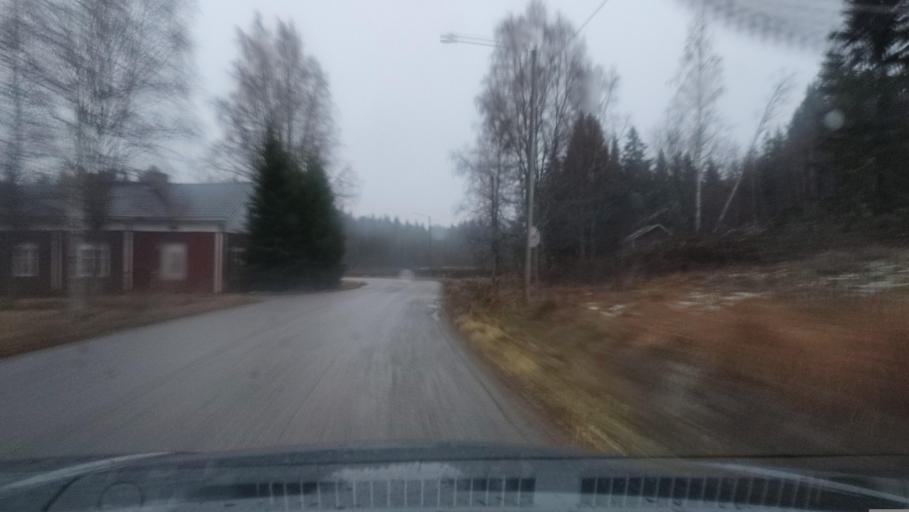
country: FI
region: Southern Ostrobothnia
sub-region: Suupohja
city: Karijoki
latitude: 62.1361
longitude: 21.5735
